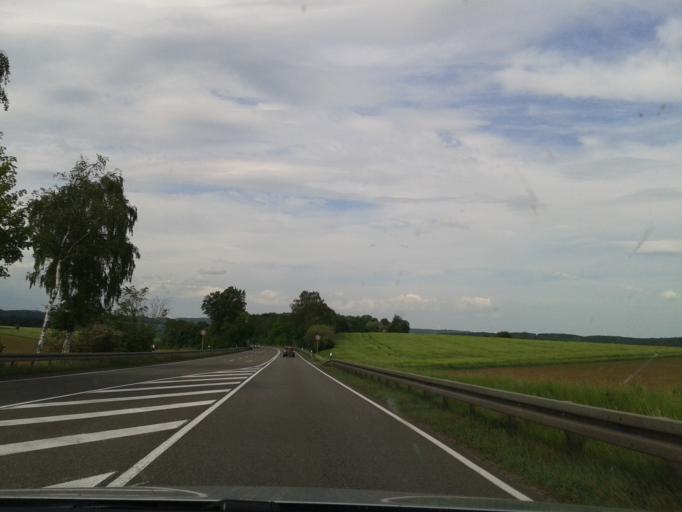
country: DE
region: Hesse
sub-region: Regierungsbezirk Kassel
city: Korbach
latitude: 51.2953
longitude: 8.8844
